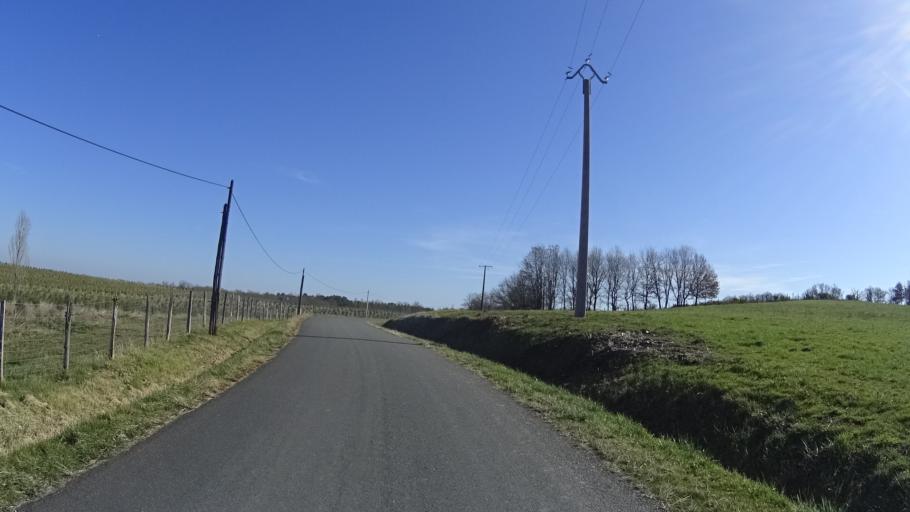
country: FR
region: Aquitaine
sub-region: Departement de la Dordogne
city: Saint-Medard-de-Mussidan
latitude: 45.1283
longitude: 0.2523
